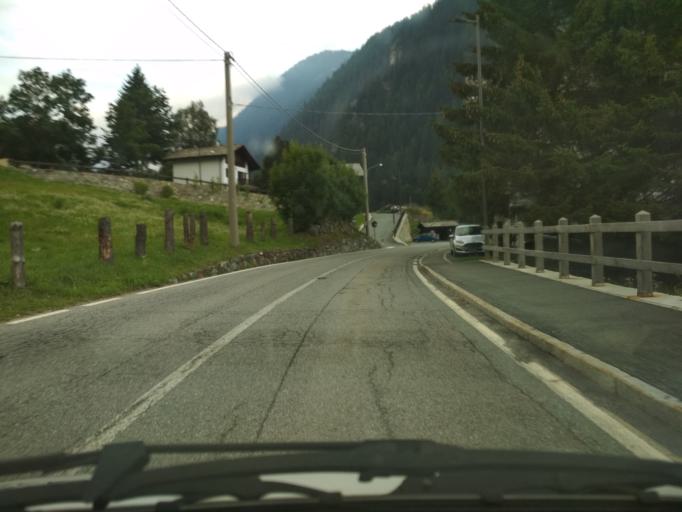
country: IT
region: Aosta Valley
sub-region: Valle d'Aosta
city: Gressoney-Saint-Jean
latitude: 45.7561
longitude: 7.8411
